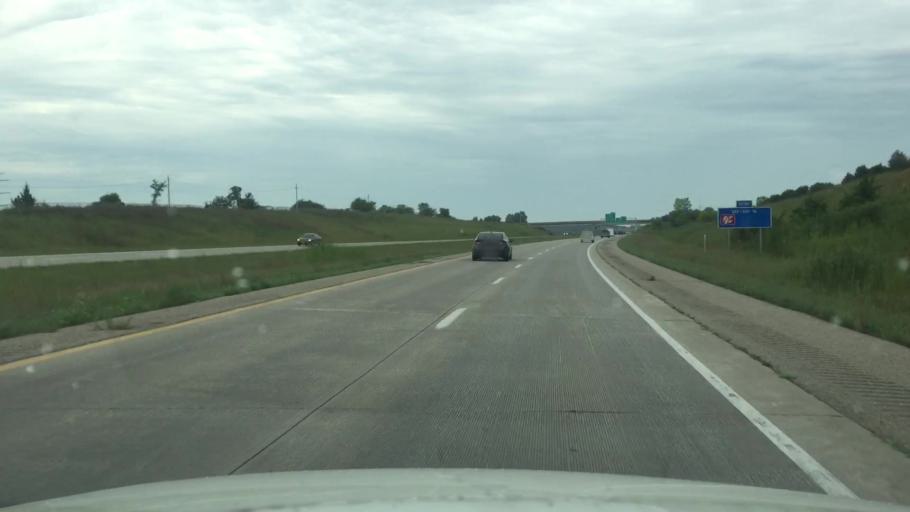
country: US
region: Iowa
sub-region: Warren County
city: Norwalk
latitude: 41.4981
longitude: -93.6099
